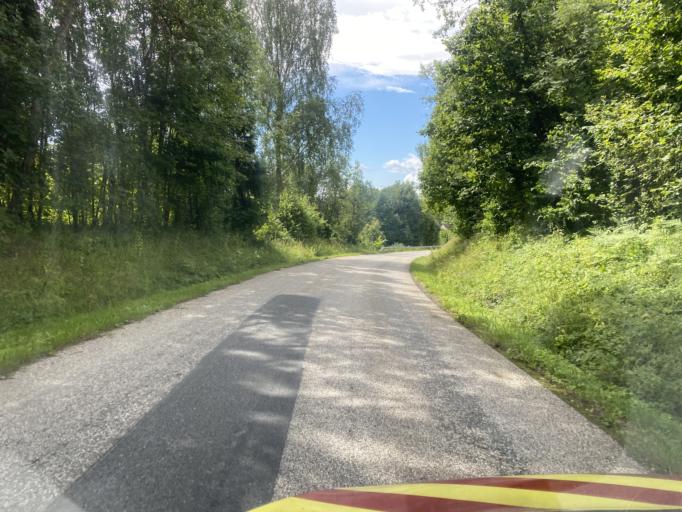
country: EE
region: Valgamaa
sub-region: Torva linn
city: Torva
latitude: 57.9480
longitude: 25.8856
